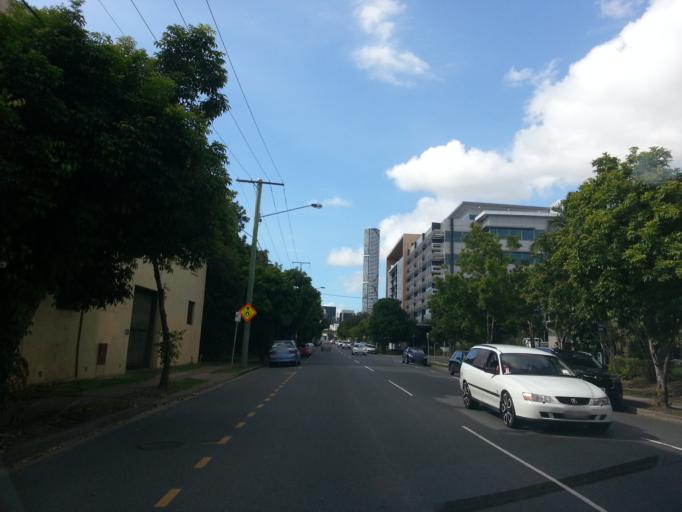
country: AU
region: Queensland
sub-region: Brisbane
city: Milton
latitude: -27.4752
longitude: 153.0100
